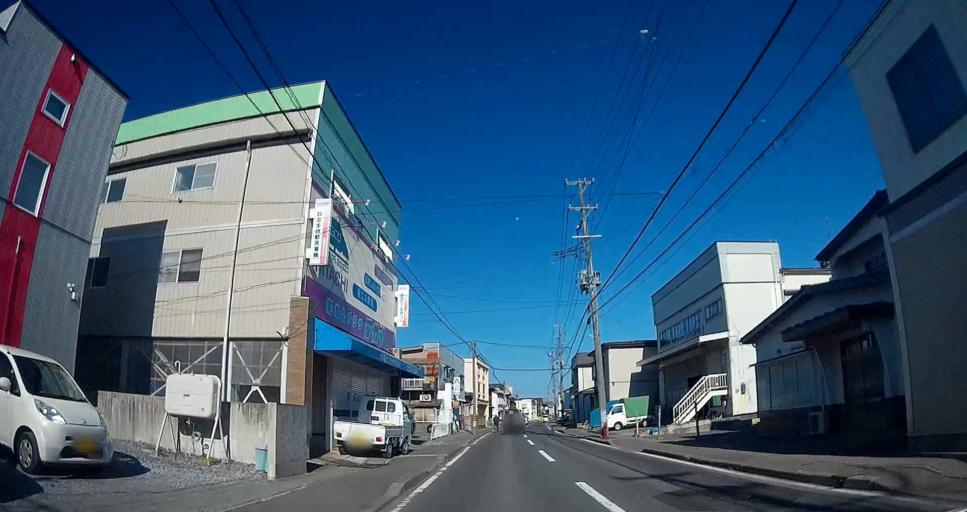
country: JP
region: Aomori
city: Hachinohe
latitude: 40.5228
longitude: 141.5367
